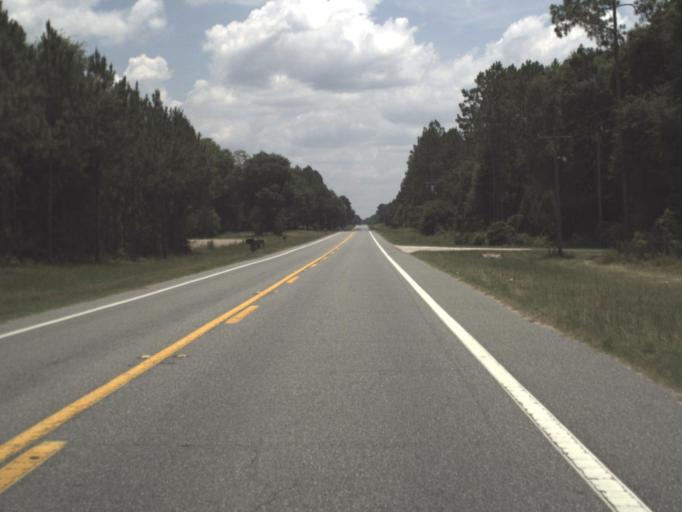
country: US
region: Florida
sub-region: Hamilton County
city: Jasper
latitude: 30.4901
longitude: -83.1266
